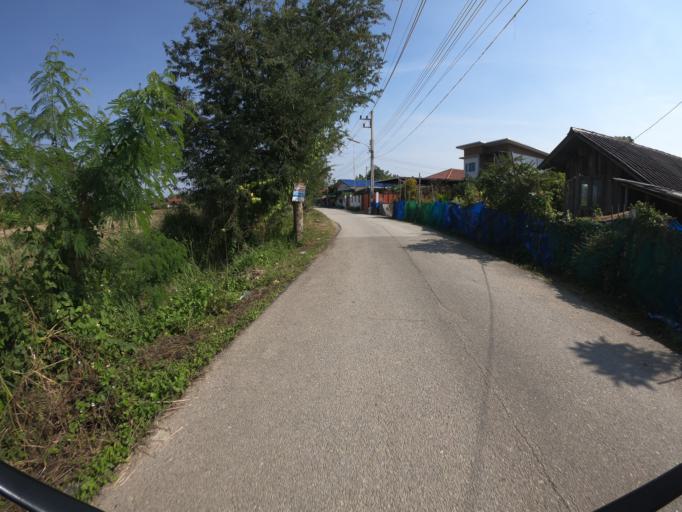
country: TH
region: Chiang Mai
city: San Sai
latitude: 18.8503
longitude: 98.9959
